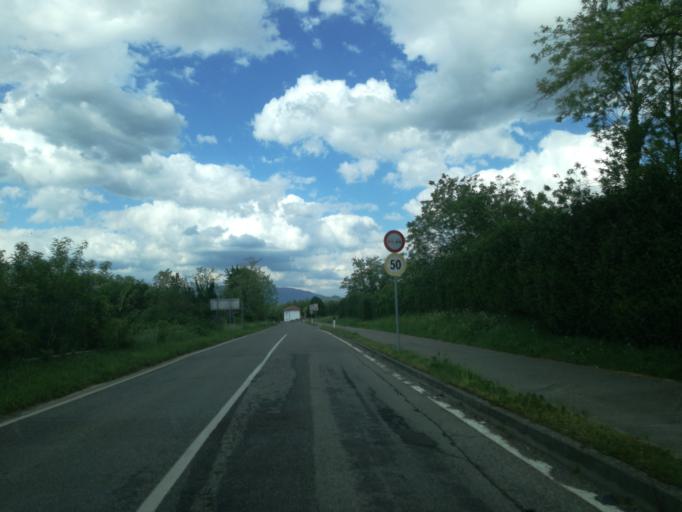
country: IT
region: Lombardy
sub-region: Provincia di Monza e Brianza
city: Ronco Briantino
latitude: 45.6606
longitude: 9.3922
